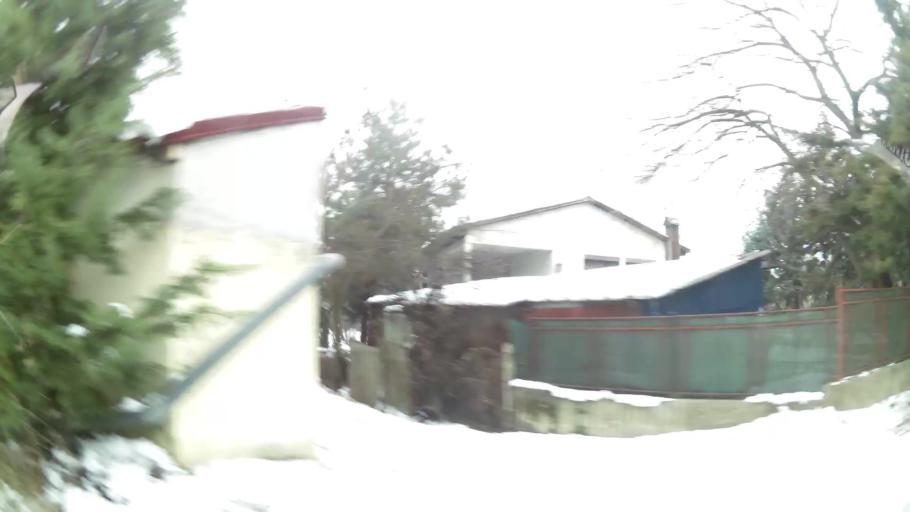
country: MK
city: Kondovo
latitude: 42.0486
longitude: 21.3428
